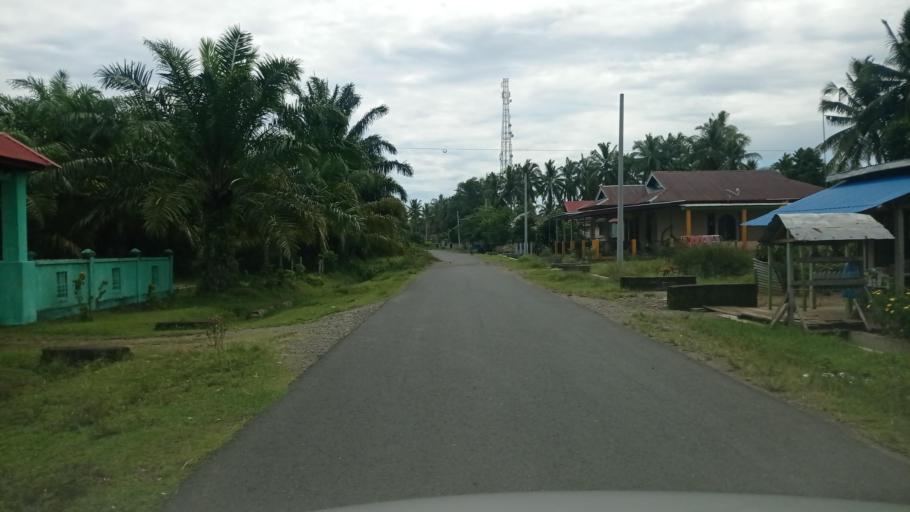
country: ID
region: Bengkulu
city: Ipuh
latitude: -2.5738
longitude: 101.1137
